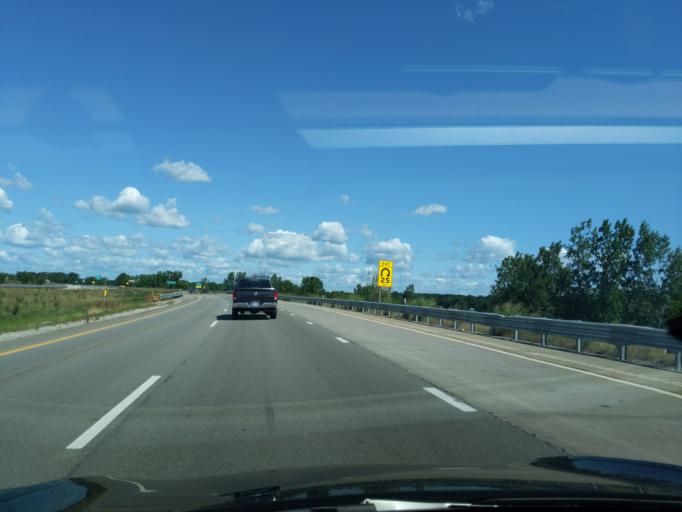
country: US
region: Michigan
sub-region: Gratiot County
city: Saint Louis
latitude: 43.3773
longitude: -84.6018
